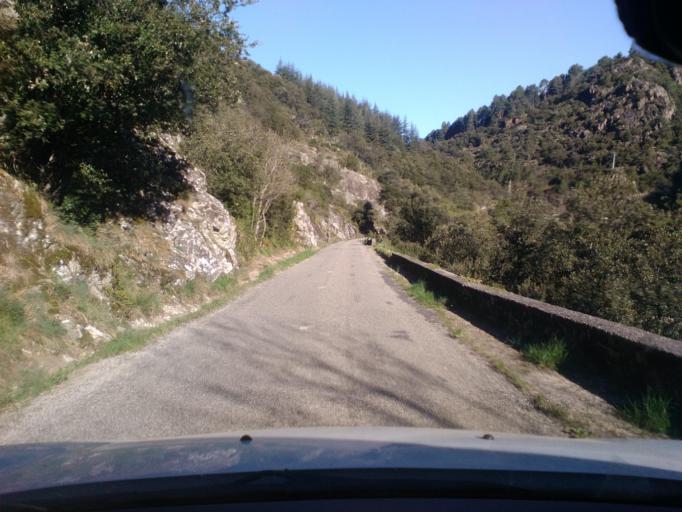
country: FR
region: Languedoc-Roussillon
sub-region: Departement du Gard
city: Lasalle
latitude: 44.1036
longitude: 3.7943
